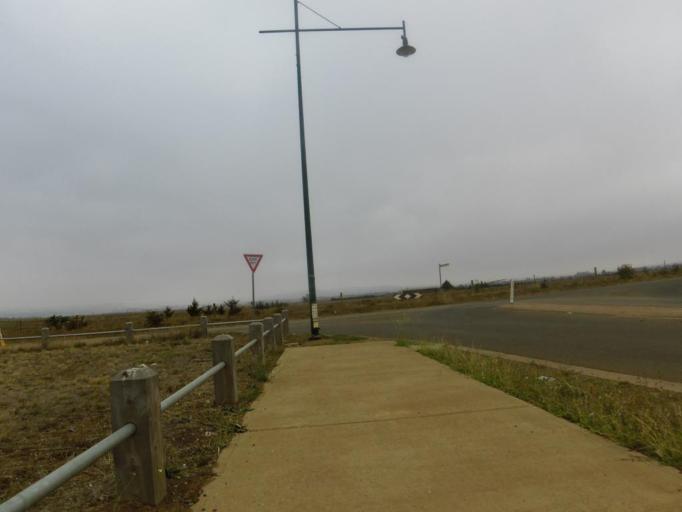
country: AU
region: Victoria
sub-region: Melton
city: Kurunjang
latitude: -37.6536
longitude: 144.5883
